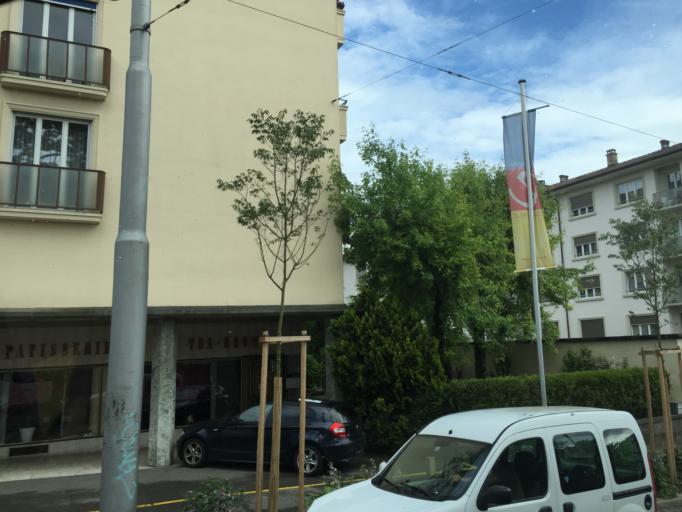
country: CH
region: Vaud
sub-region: Lausanne District
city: Lausanne
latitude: 46.5270
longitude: 6.6271
